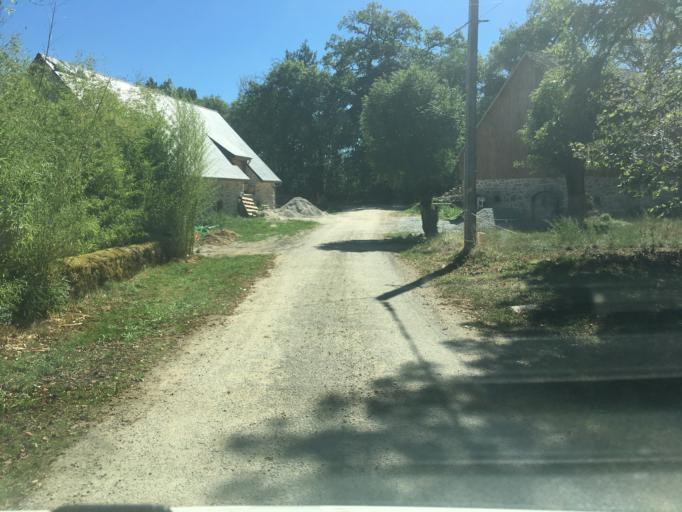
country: FR
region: Limousin
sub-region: Departement de la Correze
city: Bort-les-Orgues
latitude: 45.4363
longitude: 2.4860
